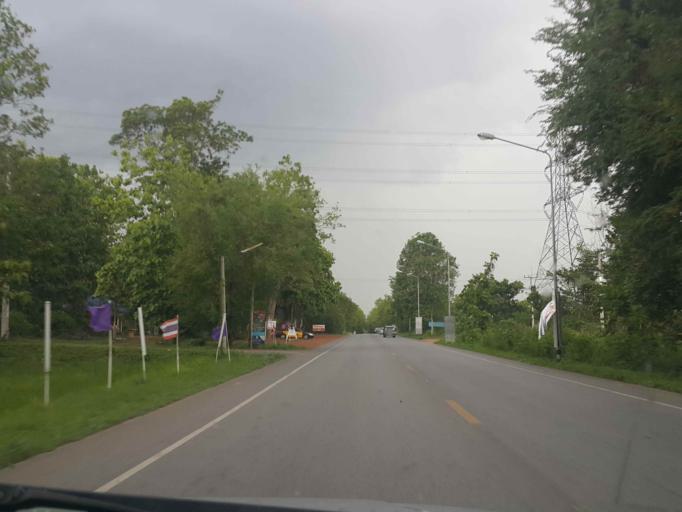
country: TH
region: Phrae
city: Den Chai
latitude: 17.9753
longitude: 100.0115
